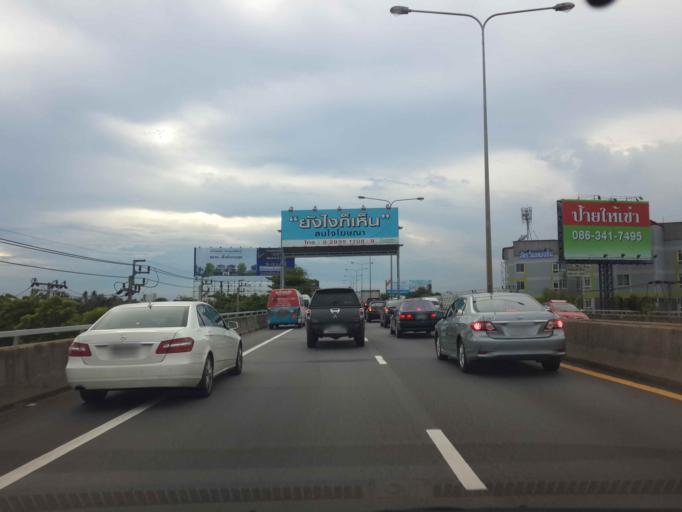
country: TH
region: Bangkok
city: Chom Thong
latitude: 13.6735
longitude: 100.4868
